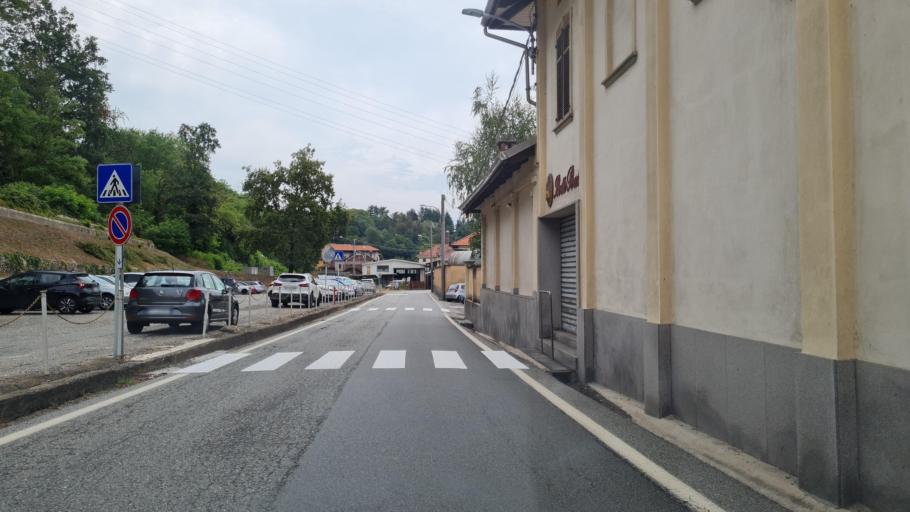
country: IT
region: Piedmont
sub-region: Provincia di Biella
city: Lessona
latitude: 45.5931
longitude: 8.1861
